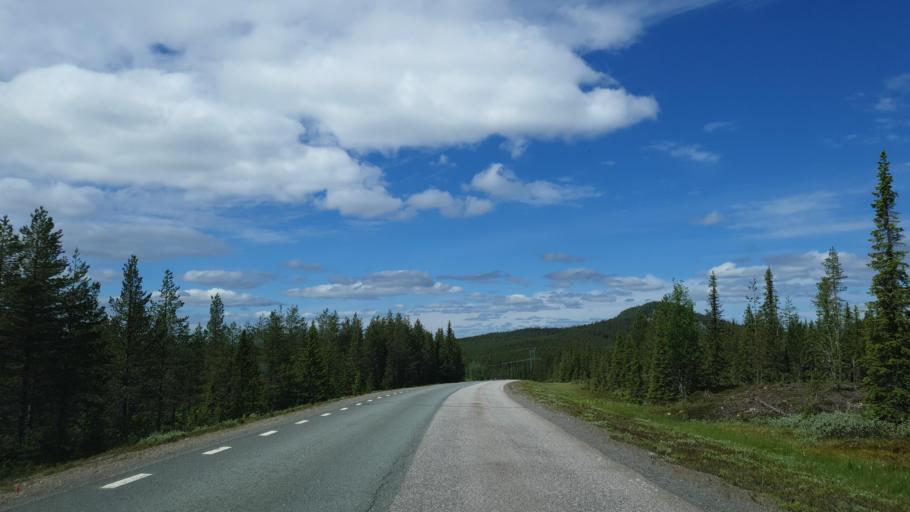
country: SE
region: Vaesterbotten
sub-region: Mala Kommun
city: Mala
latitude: 65.5719
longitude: 18.3494
